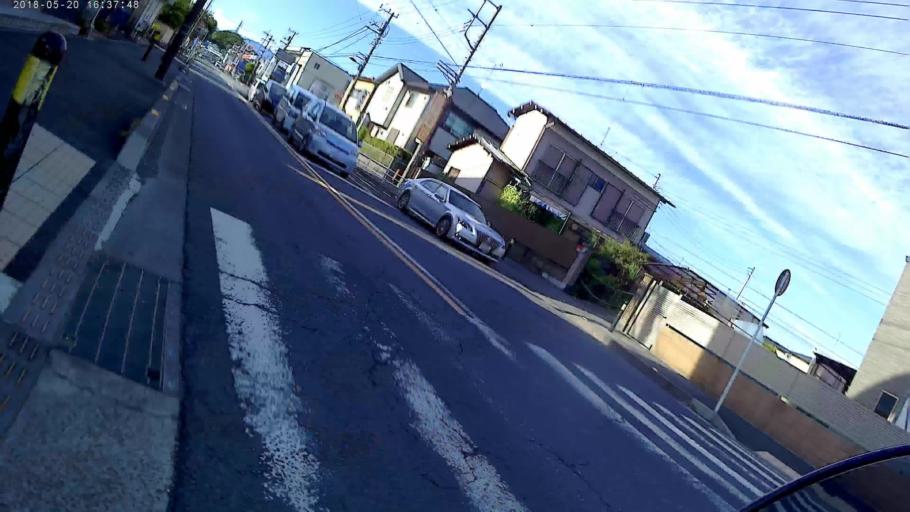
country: JP
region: Kanagawa
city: Odawara
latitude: 35.2680
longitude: 139.1591
